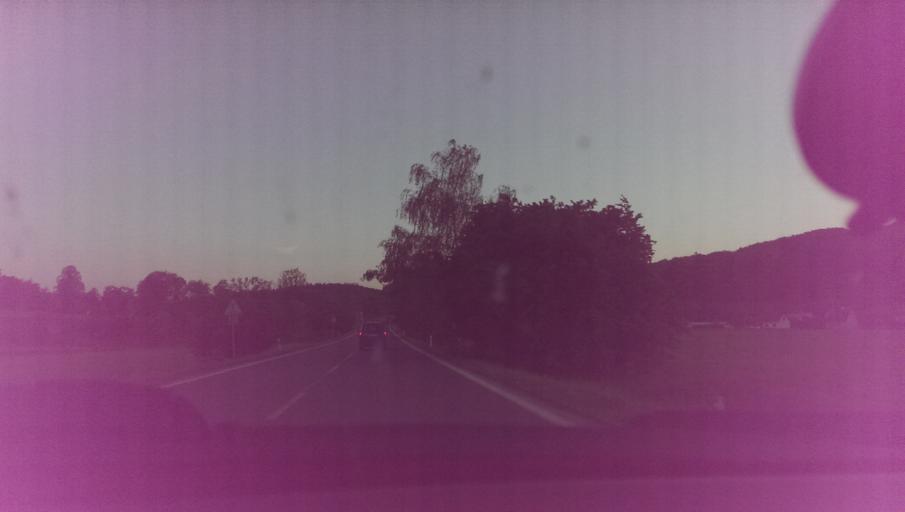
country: CZ
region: Zlin
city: Valasska Polanka
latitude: 49.2722
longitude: 17.9992
